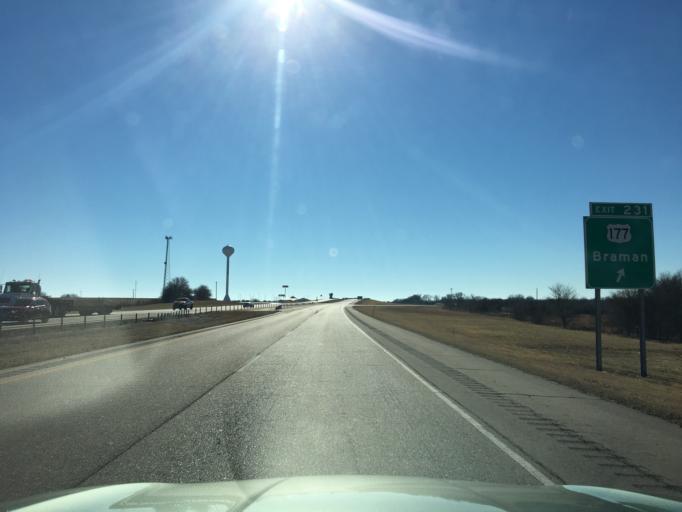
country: US
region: Oklahoma
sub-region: Kay County
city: Blackwell
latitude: 36.9468
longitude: -97.3458
